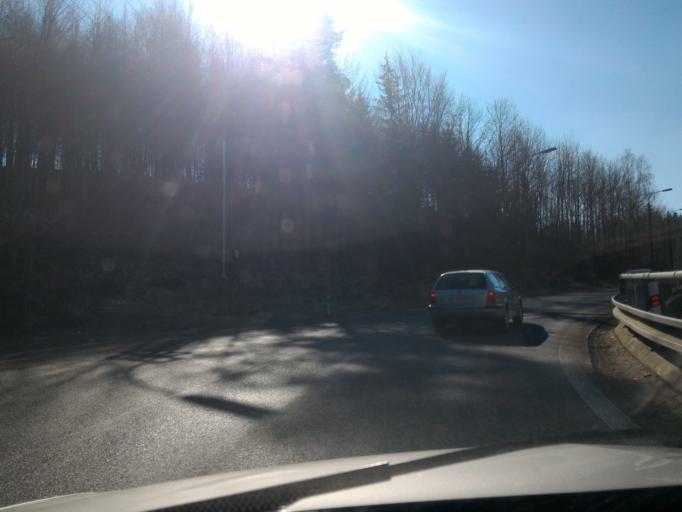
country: CZ
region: Liberecky
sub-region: Okres Jablonec nad Nisou
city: Lucany nad Nisou
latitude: 50.7403
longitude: 15.2307
